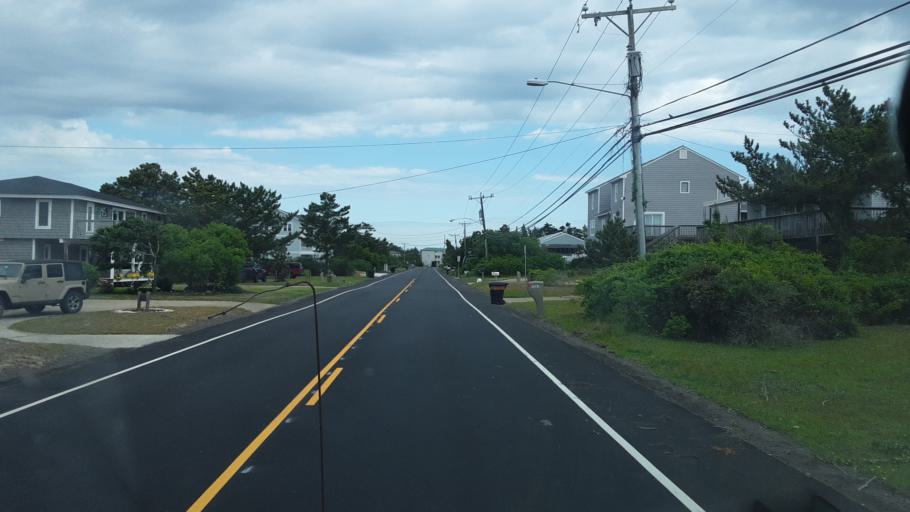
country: US
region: Virginia
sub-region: City of Virginia Beach
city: Virginia Beach
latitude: 36.7136
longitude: -75.9333
